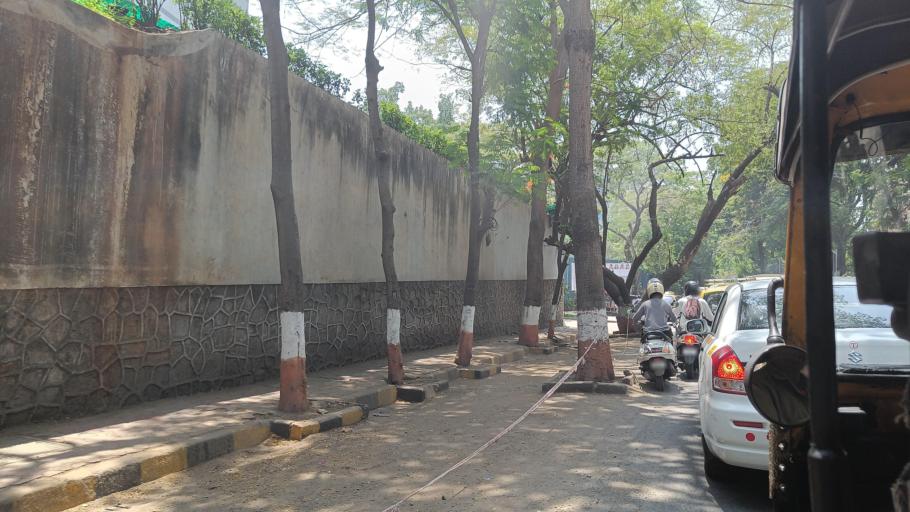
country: IN
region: Maharashtra
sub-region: Mumbai Suburban
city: Mumbai
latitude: 19.0773
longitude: 72.8505
